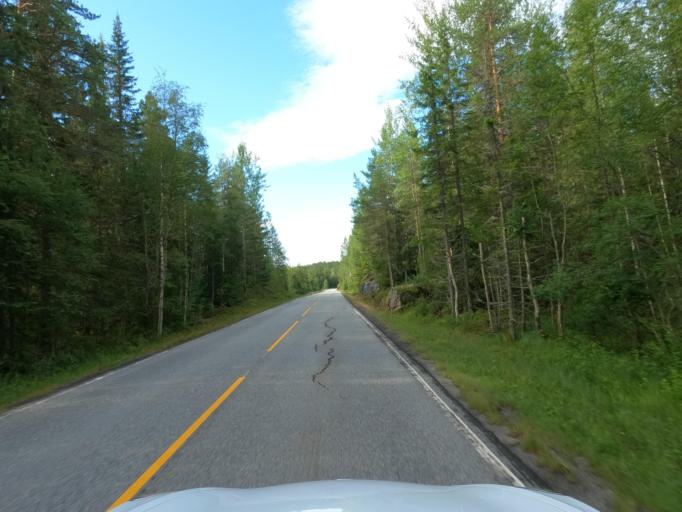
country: NO
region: Telemark
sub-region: Notodden
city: Notodden
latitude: 59.7286
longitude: 9.2975
